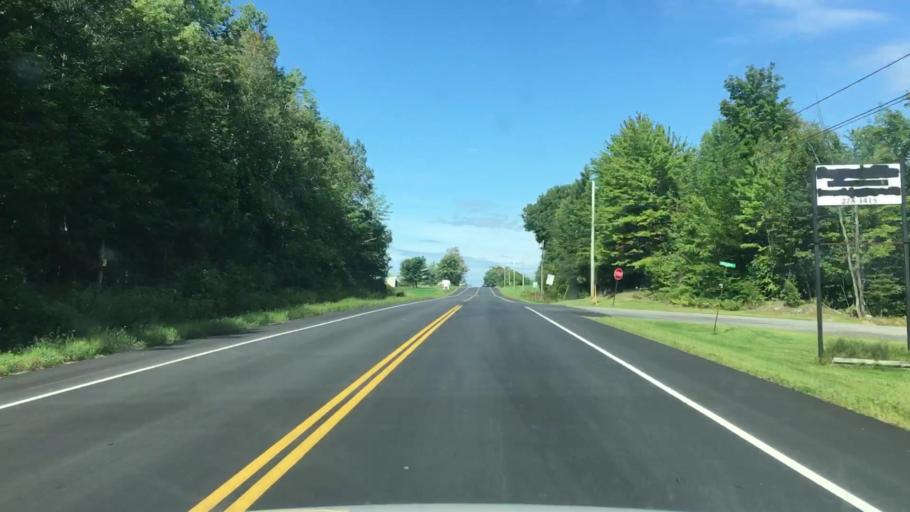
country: US
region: Maine
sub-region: Penobscot County
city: Corinna
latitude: 44.9515
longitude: -69.2527
